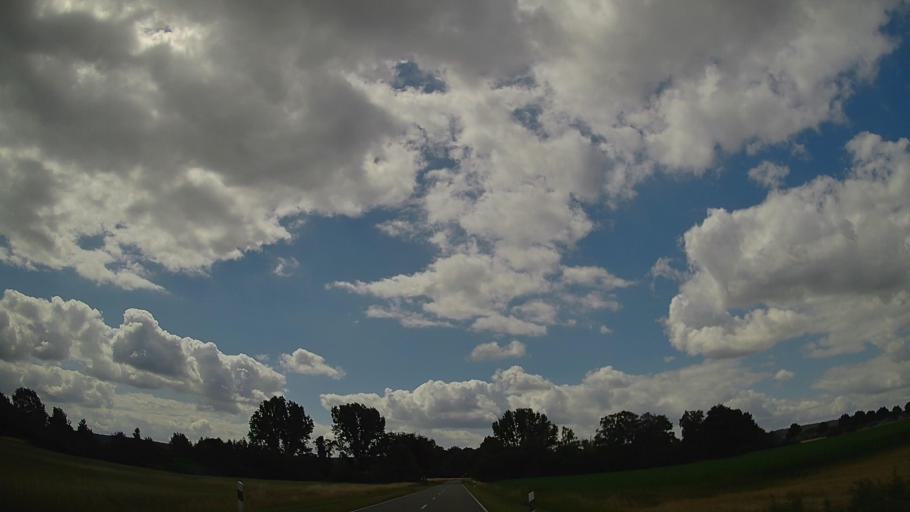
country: DE
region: Lower Saxony
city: Brockum
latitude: 52.4772
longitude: 8.4307
